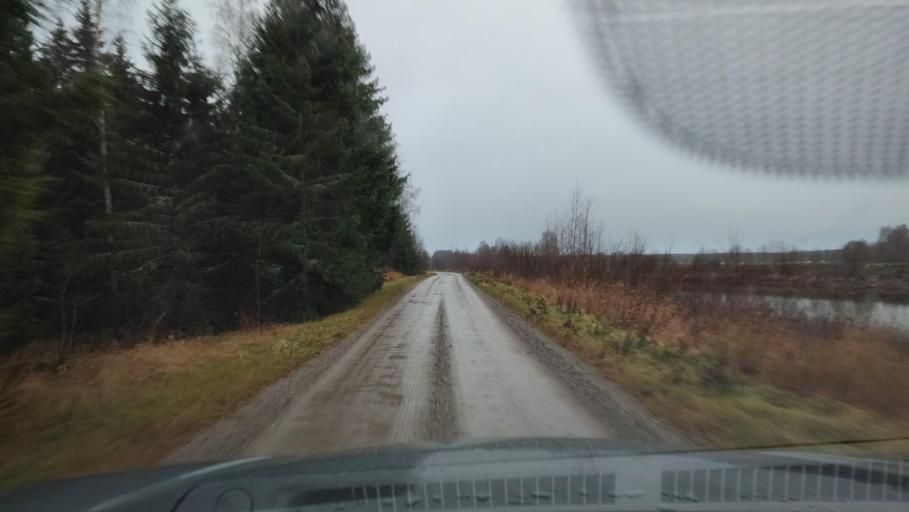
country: FI
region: Ostrobothnia
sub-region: Sydosterbotten
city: Kristinestad
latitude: 62.2392
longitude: 21.4690
